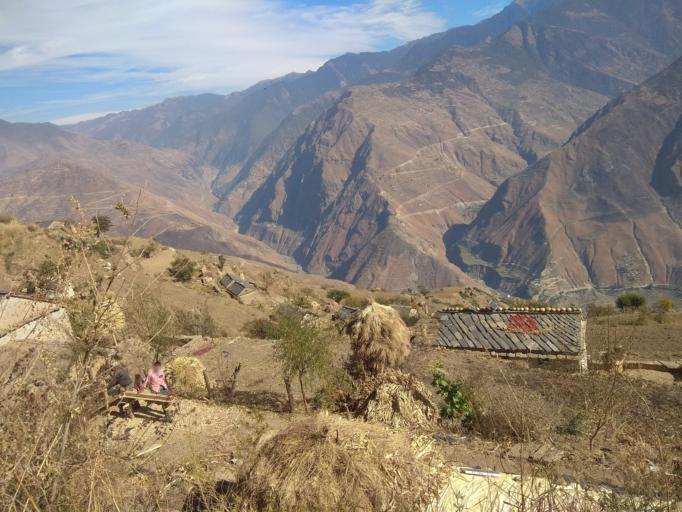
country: NP
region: Mid Western
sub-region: Karnali Zone
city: Jumla
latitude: 29.3086
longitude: 81.7282
